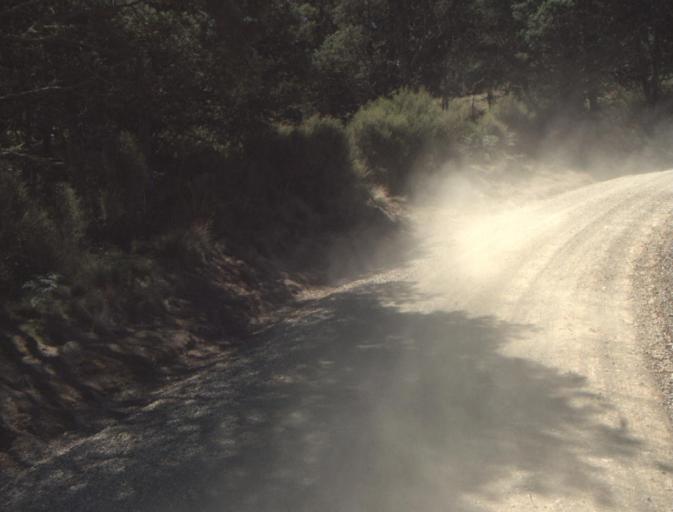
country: AU
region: Tasmania
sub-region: Dorset
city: Scottsdale
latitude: -41.3144
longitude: 147.4638
